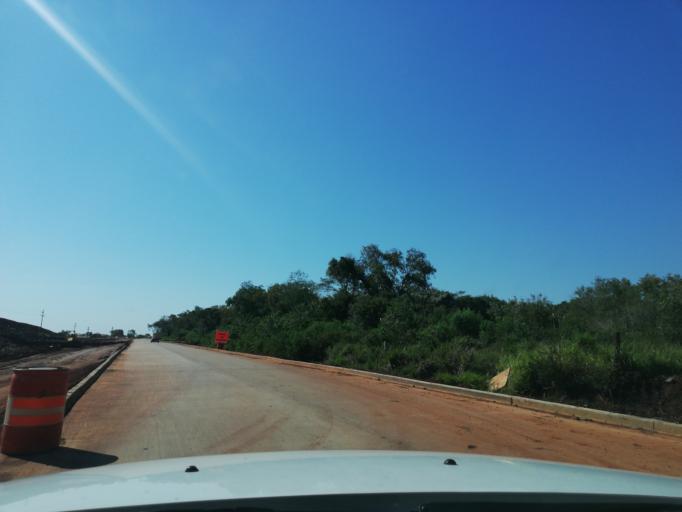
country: AR
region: Misiones
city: Santa Ana
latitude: -27.4170
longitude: -55.6120
